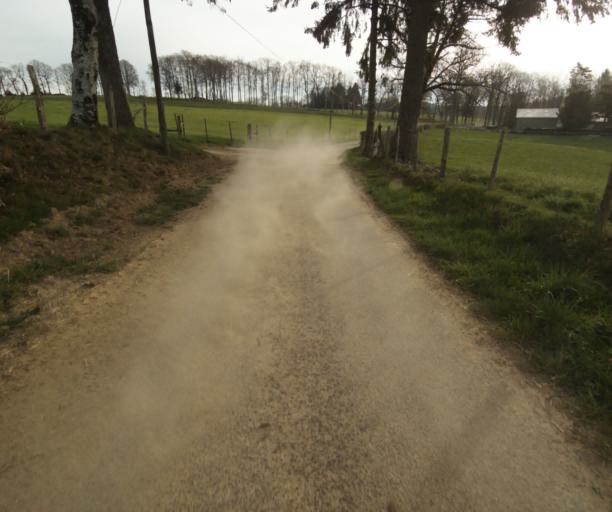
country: FR
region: Limousin
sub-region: Departement de la Correze
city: Chamboulive
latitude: 45.4521
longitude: 1.7535
